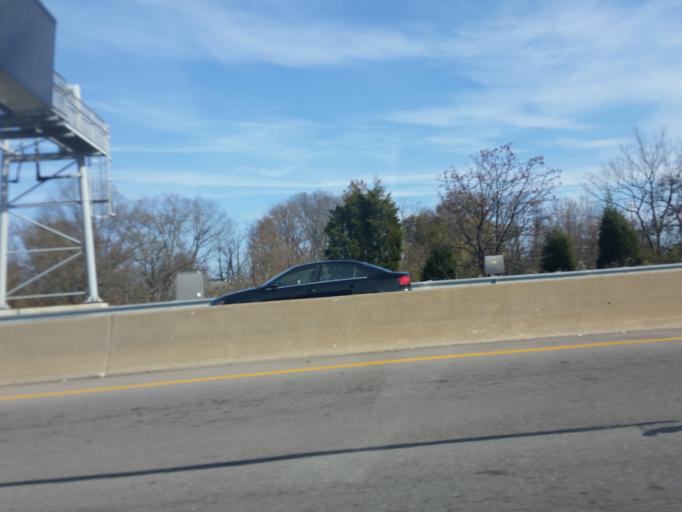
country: US
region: Kentucky
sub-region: Campbell County
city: Highland Heights
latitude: 39.0379
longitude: -84.4541
